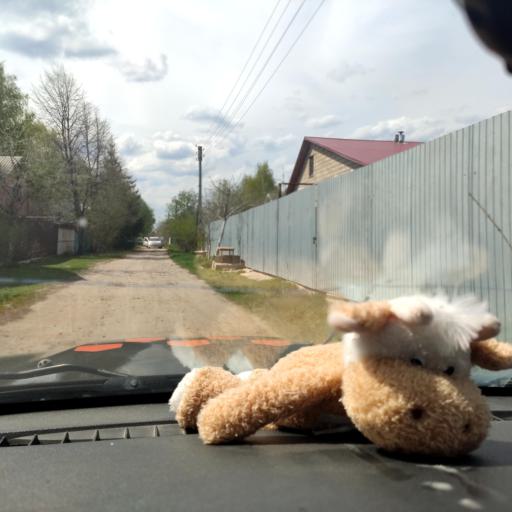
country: RU
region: Samara
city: Podstepki
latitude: 53.5111
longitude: 49.0814
